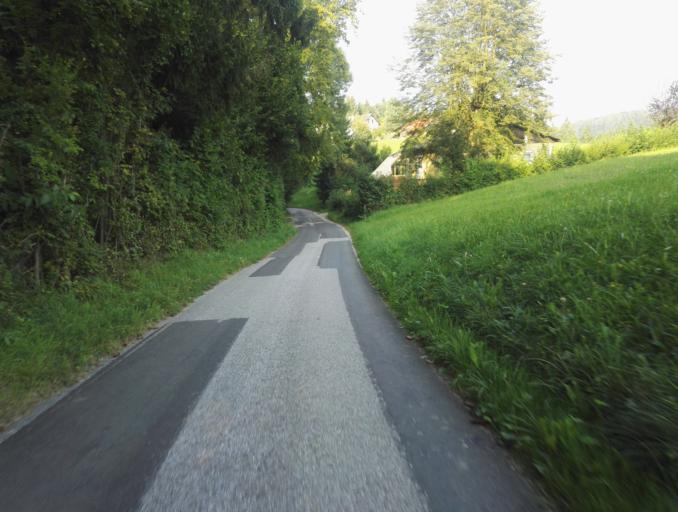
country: AT
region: Styria
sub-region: Politischer Bezirk Graz-Umgebung
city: Sankt Oswald bei Plankenwarth
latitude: 47.0929
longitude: 15.2845
